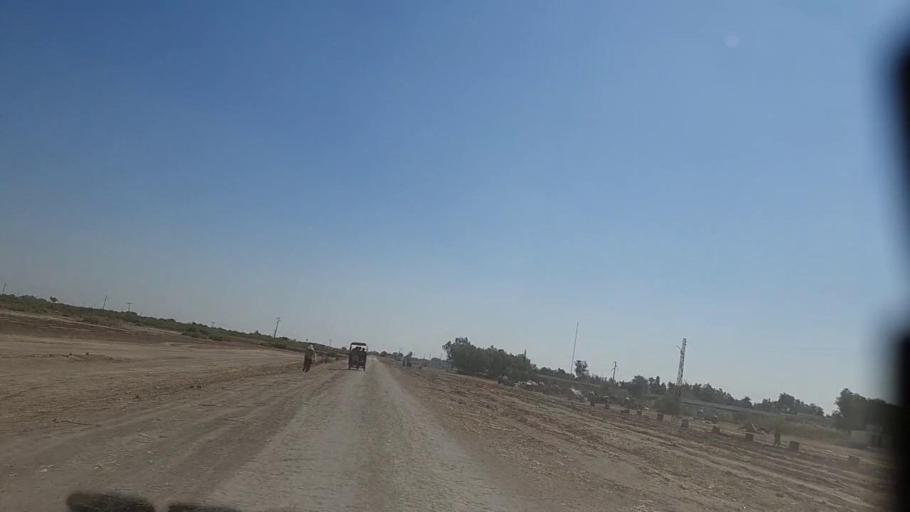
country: PK
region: Sindh
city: Digri
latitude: 25.1617
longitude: 69.0402
